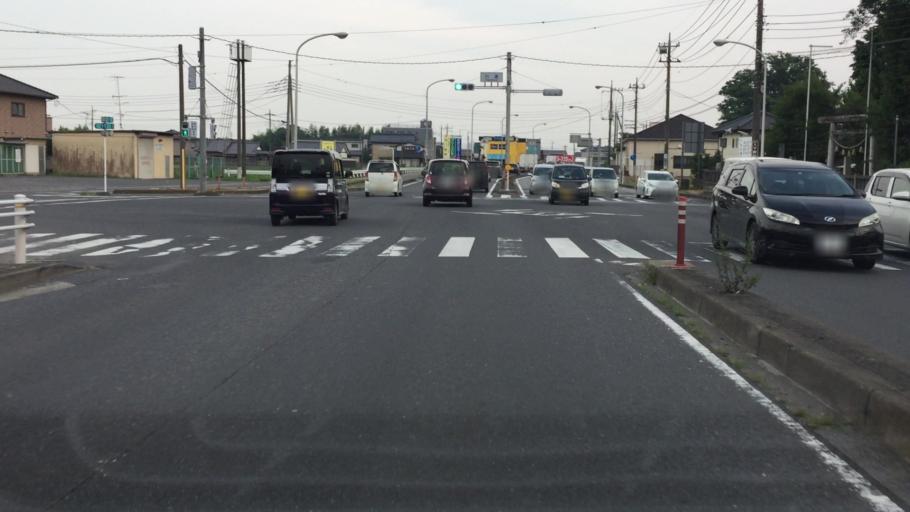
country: JP
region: Tochigi
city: Tochigi
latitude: 36.3625
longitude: 139.7168
